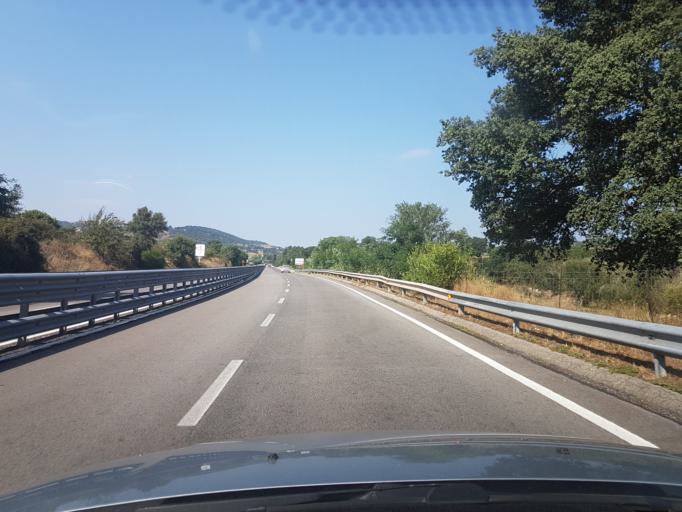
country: IT
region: Sardinia
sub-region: Provincia di Nuoro
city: Oniferi
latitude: 40.3157
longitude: 9.2224
